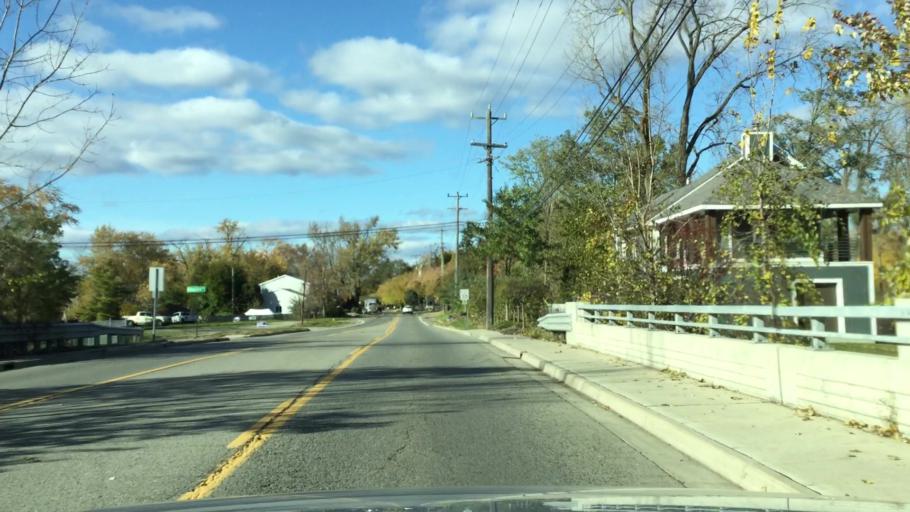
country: US
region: Michigan
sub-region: Oakland County
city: Keego Harbor
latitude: 42.6178
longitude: -83.3505
